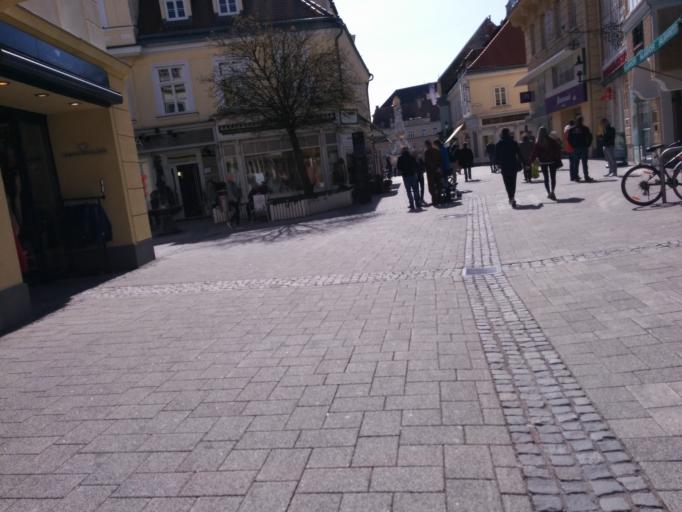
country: AT
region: Lower Austria
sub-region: Politischer Bezirk Baden
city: Baden
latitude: 48.0087
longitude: 16.2340
